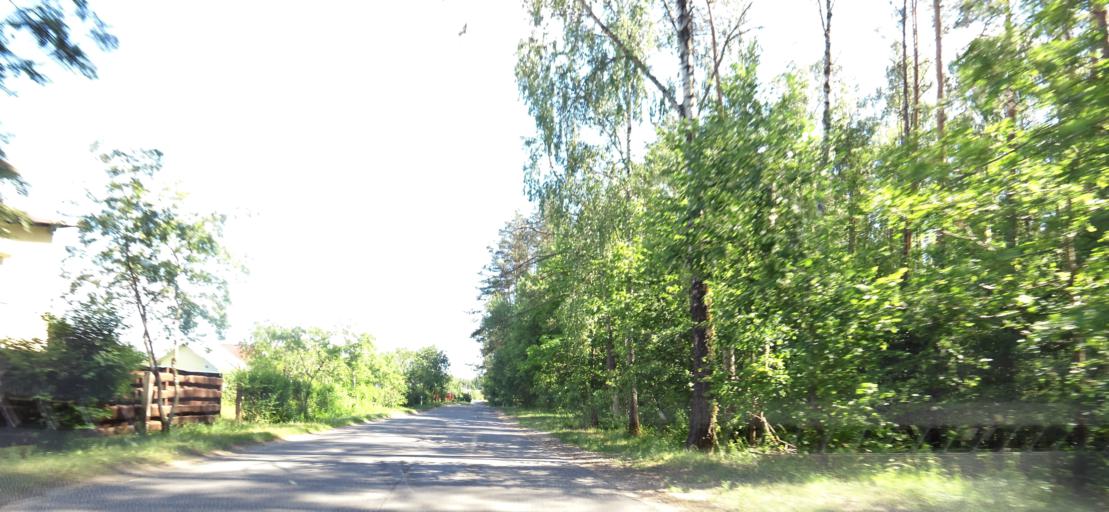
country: LT
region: Vilnius County
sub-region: Vilnius
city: Fabijoniskes
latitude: 54.8020
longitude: 25.3308
